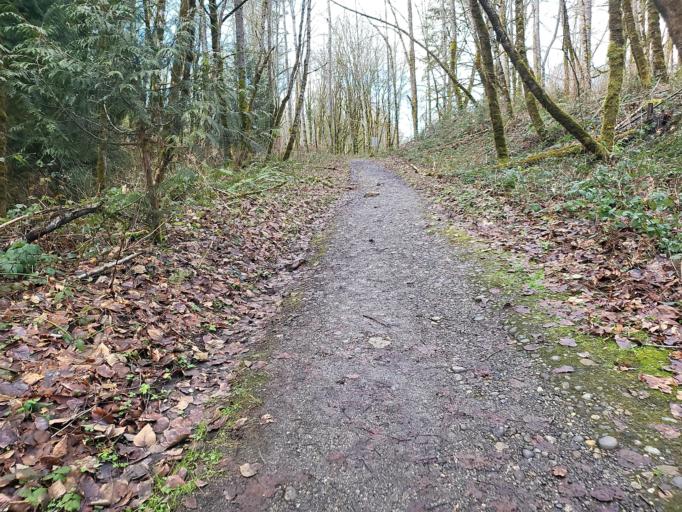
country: US
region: Washington
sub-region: King County
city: Newcastle
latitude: 47.5330
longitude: -122.1285
